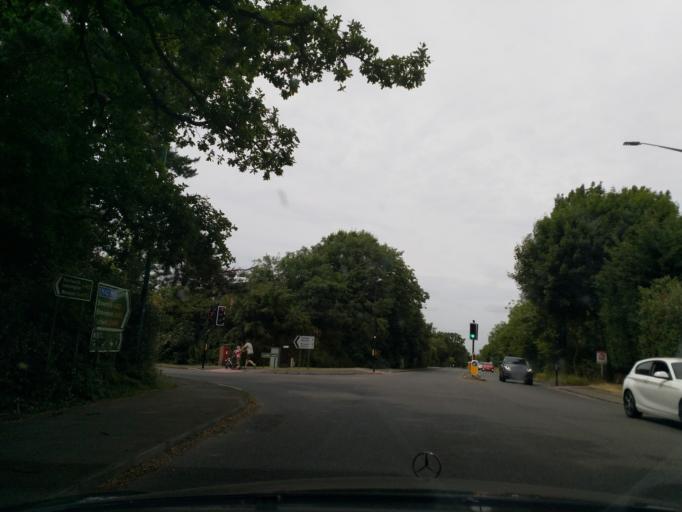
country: GB
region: England
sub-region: Solihull
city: Balsall Common
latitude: 52.3837
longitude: -1.6445
